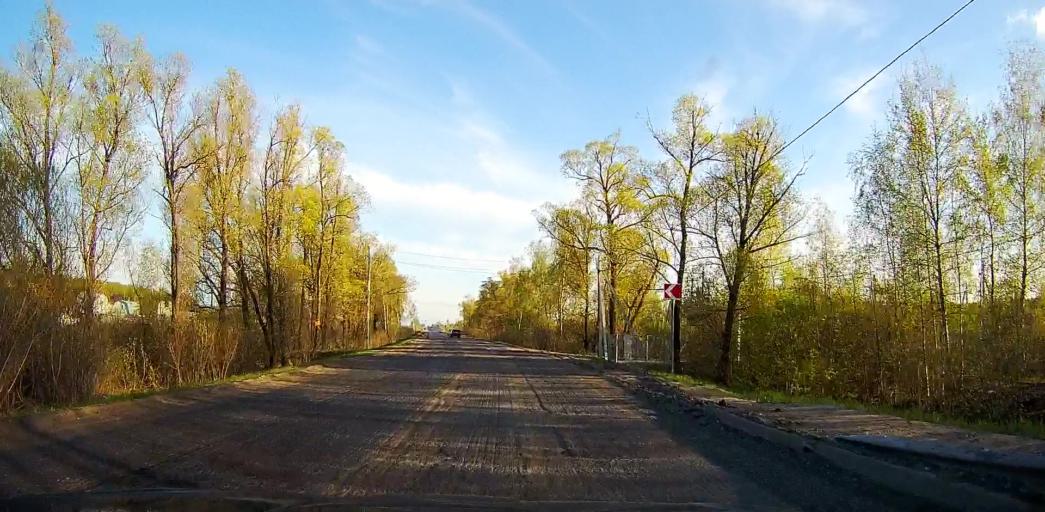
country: RU
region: Moskovskaya
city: Bronnitsy
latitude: 55.3015
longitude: 38.2101
